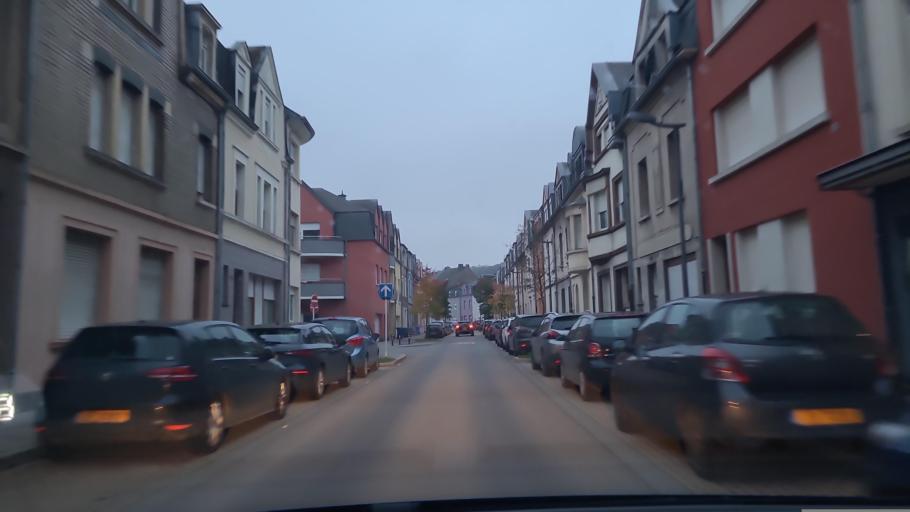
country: LU
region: Luxembourg
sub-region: Canton d'Esch-sur-Alzette
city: Obercorn
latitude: 49.5187
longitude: 5.8961
